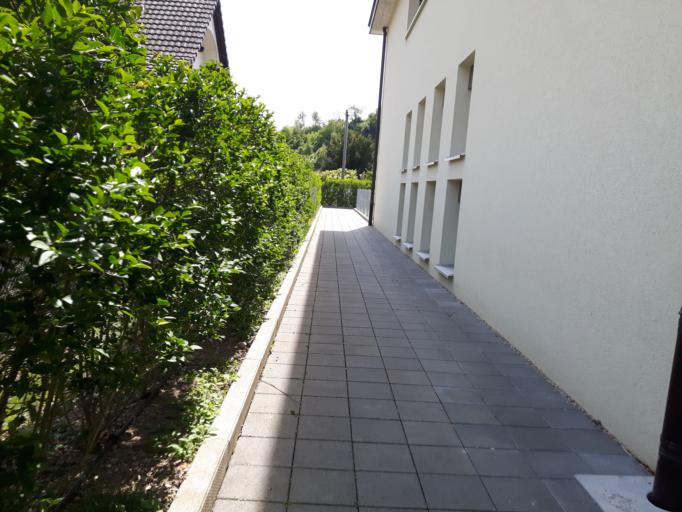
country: CH
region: Neuchatel
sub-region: Boudry District
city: Cortaillod
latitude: 46.9464
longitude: 6.8527
